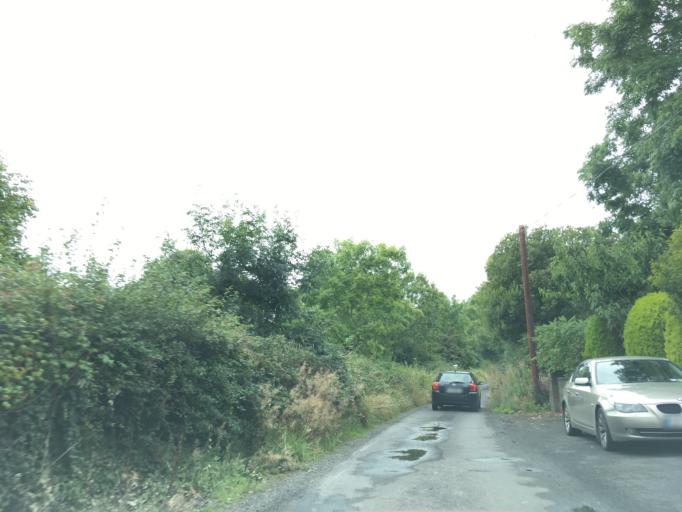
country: IE
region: Munster
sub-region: An Clar
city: Ennis
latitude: 52.7278
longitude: -9.0700
